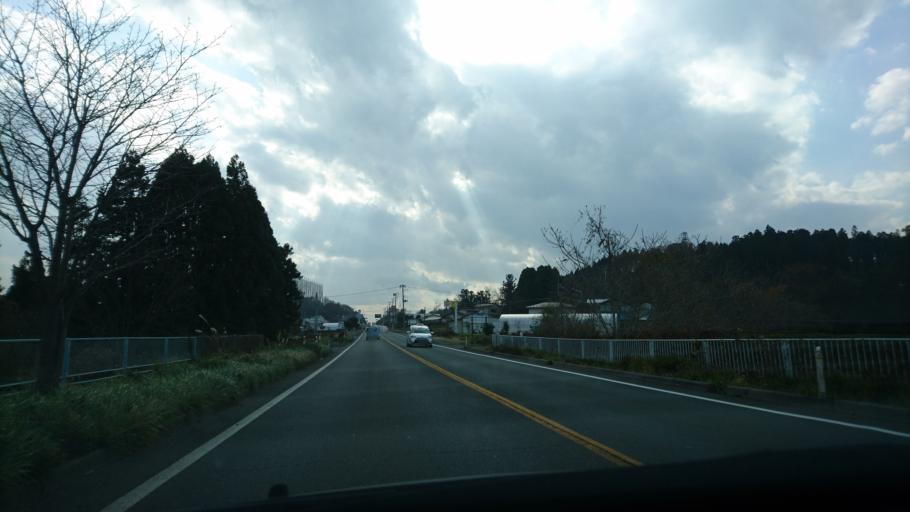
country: JP
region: Iwate
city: Mizusawa
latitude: 39.0360
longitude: 141.1184
